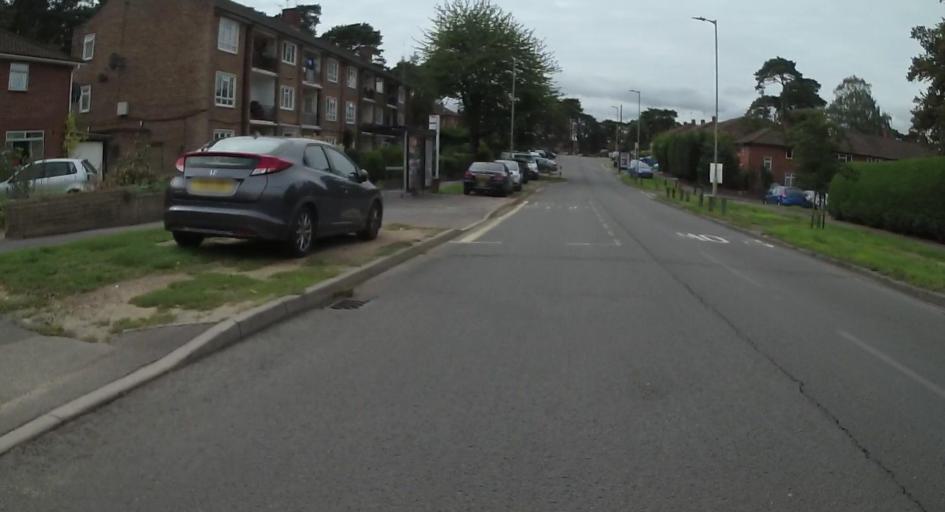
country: GB
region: England
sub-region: Surrey
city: West Byfleet
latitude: 51.3319
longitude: -0.5267
